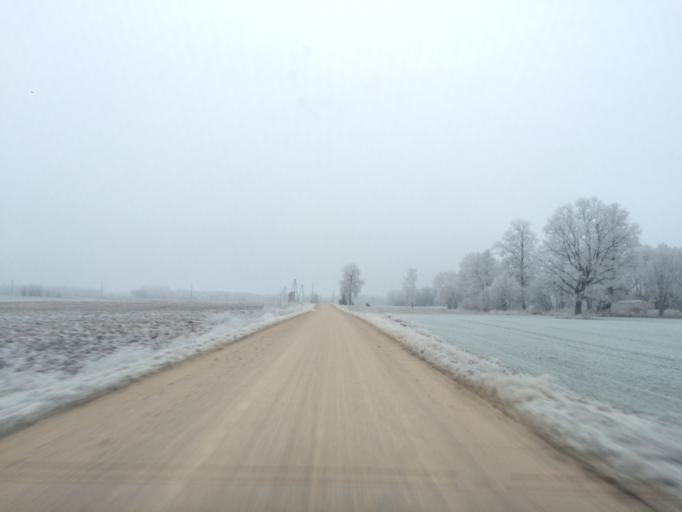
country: LV
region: Ludzas Rajons
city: Ludza
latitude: 56.6030
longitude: 27.5178
